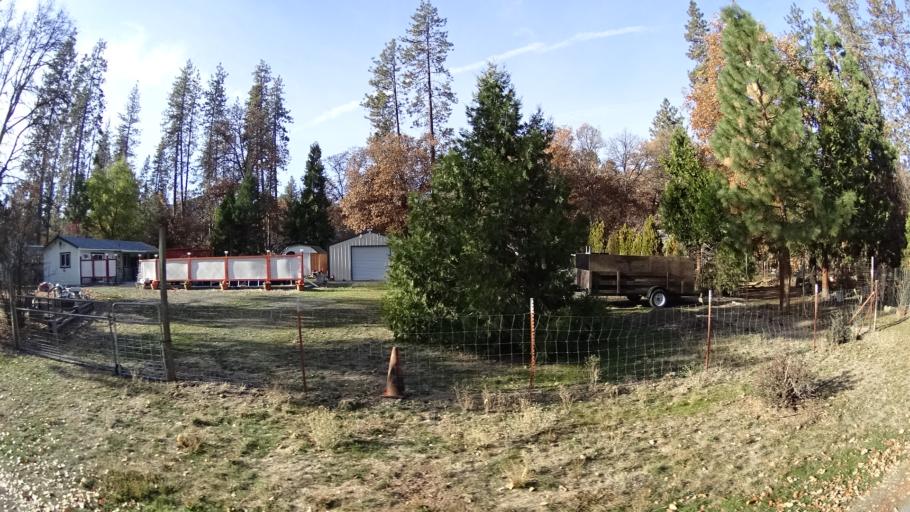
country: US
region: California
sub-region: Siskiyou County
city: Yreka
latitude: 41.6839
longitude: -122.6399
